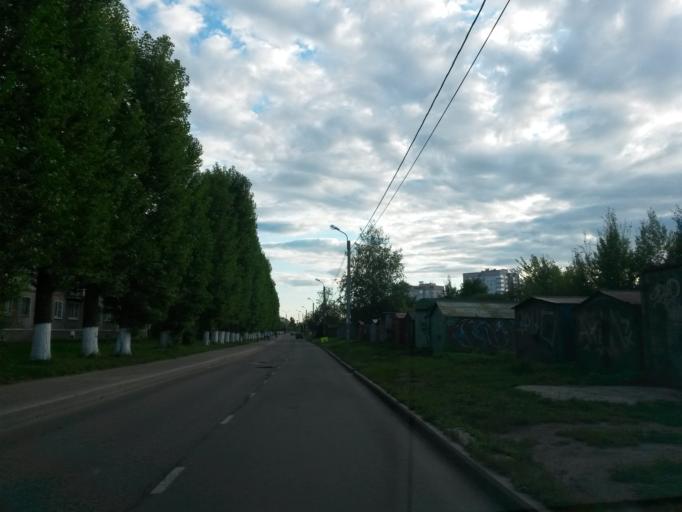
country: RU
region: Jaroslavl
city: Yaroslavl
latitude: 57.6861
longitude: 39.7725
